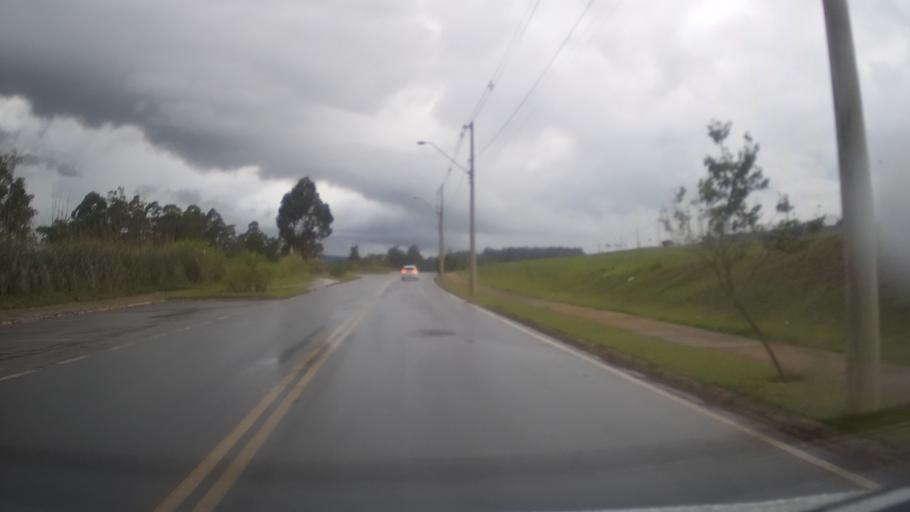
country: BR
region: Sao Paulo
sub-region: Itupeva
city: Itupeva
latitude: -23.1805
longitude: -47.0475
